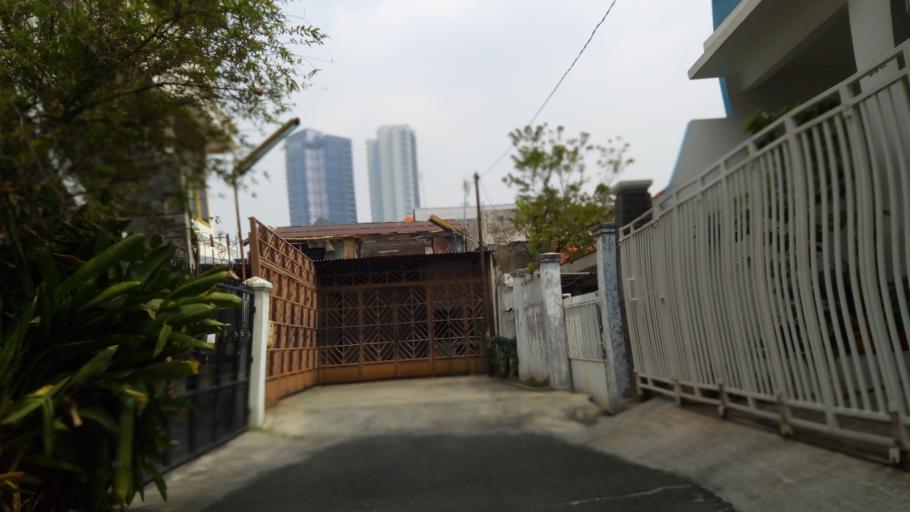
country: ID
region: Jakarta Raya
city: Jakarta
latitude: -6.1611
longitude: 106.8361
